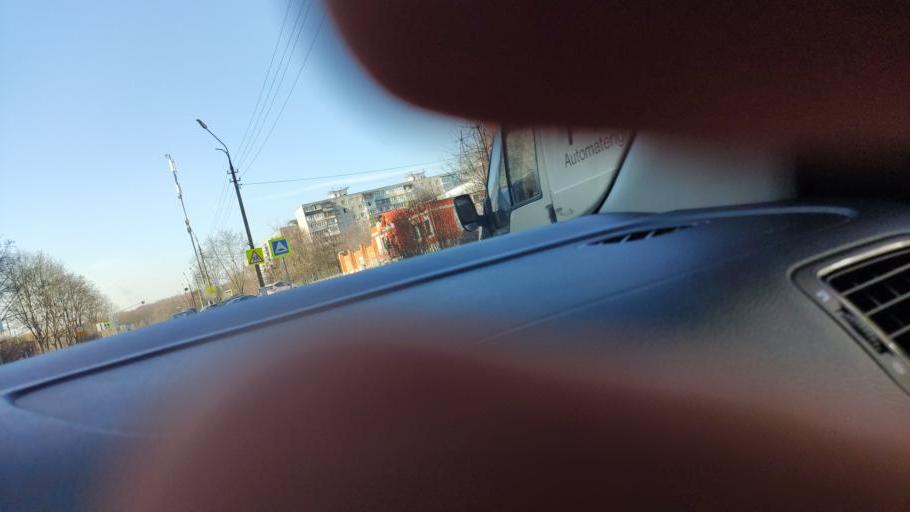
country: RU
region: Moskovskaya
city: Elektrostal'
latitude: 55.7680
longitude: 38.4255
